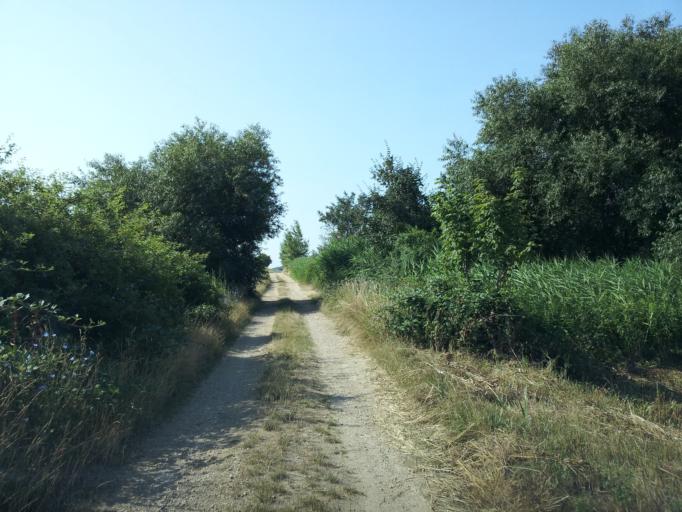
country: HU
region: Zala
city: Cserszegtomaj
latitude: 46.8472
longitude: 17.2309
